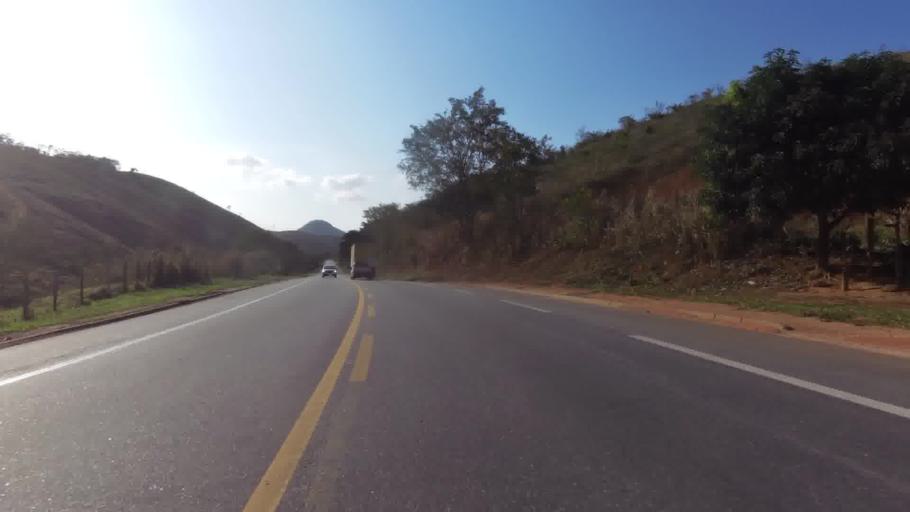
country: BR
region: Espirito Santo
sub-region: Mimoso Do Sul
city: Mimoso do Sul
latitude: -21.1861
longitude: -41.2931
